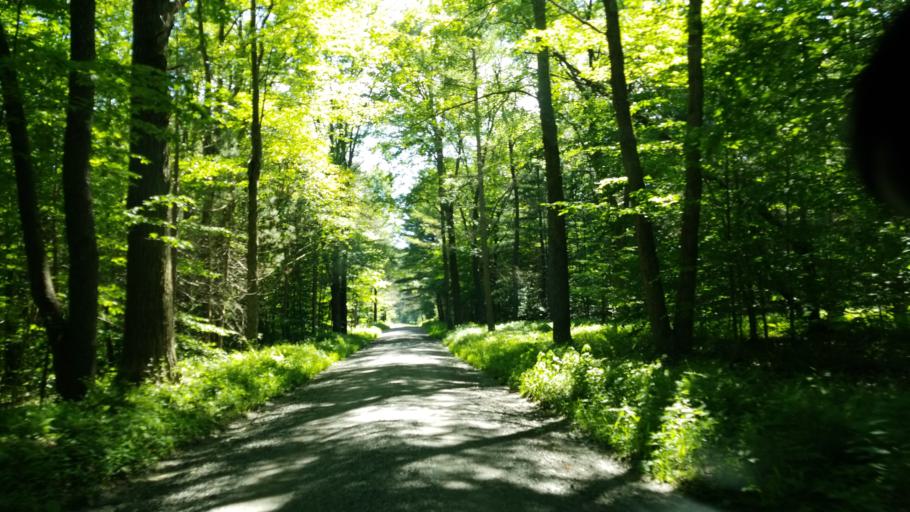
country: US
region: Pennsylvania
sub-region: Clearfield County
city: Clearfield
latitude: 41.2053
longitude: -78.4201
